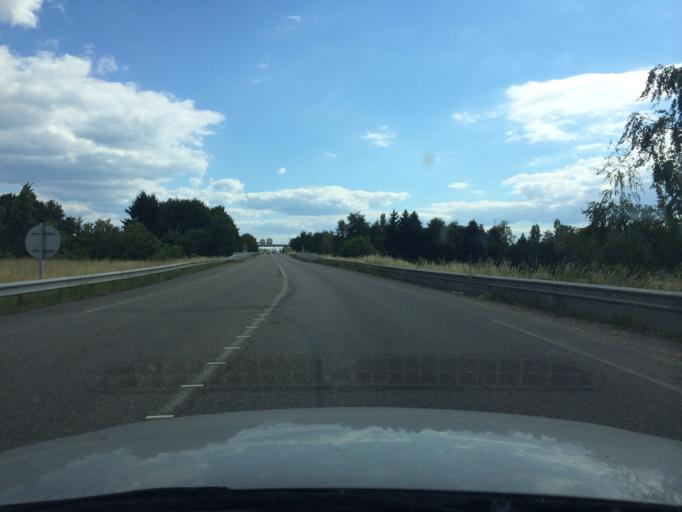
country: FR
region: Lorraine
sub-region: Departement de la Moselle
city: Phalsbourg
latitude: 48.7764
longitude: 7.2433
